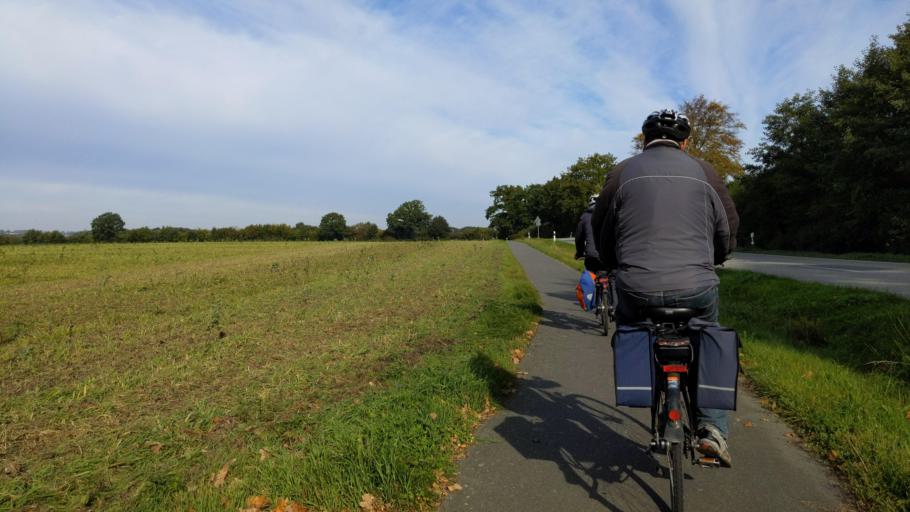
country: DE
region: Schleswig-Holstein
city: Wesenberg
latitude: 53.8569
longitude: 10.5406
